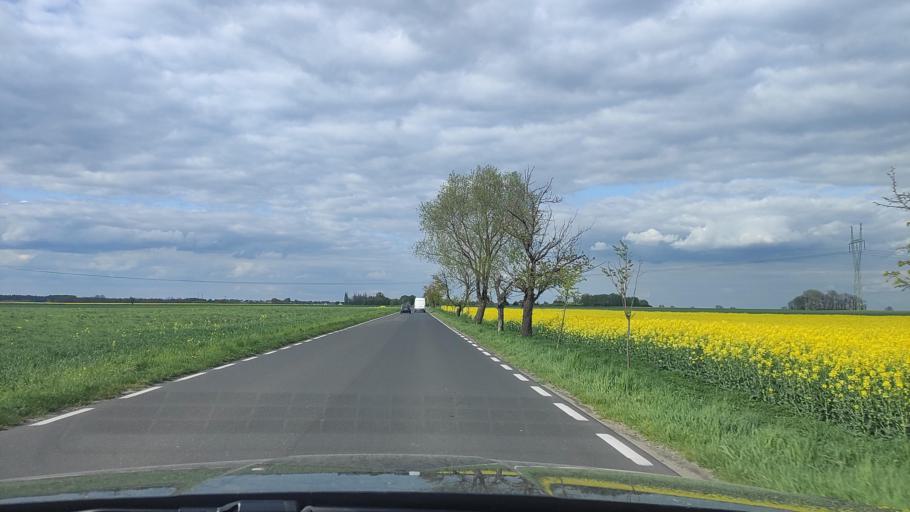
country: PL
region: Greater Poland Voivodeship
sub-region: Powiat poznanski
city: Kostrzyn
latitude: 52.4355
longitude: 17.1636
